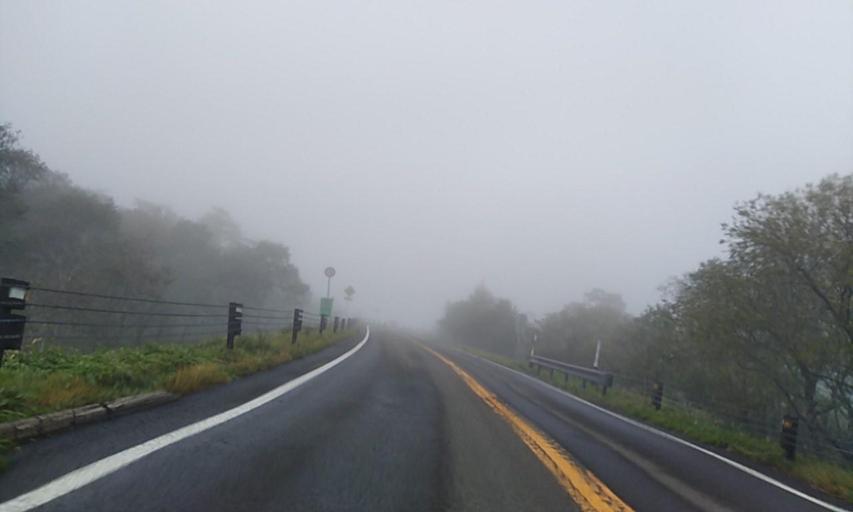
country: JP
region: Hokkaido
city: Bihoro
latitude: 43.5517
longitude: 144.5050
